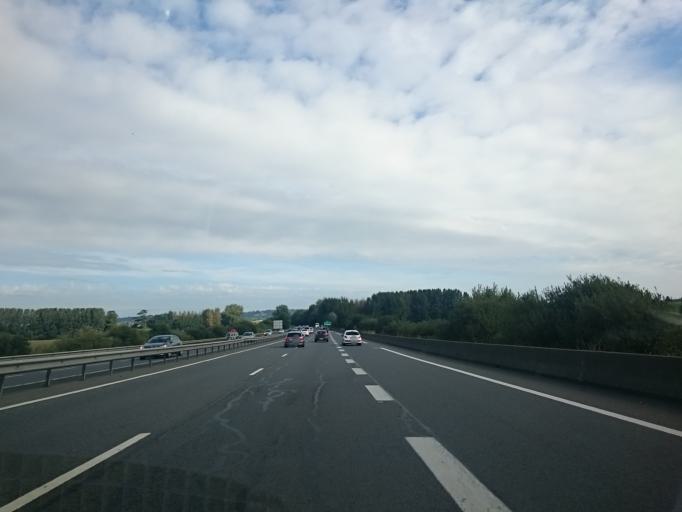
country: FR
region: Lower Normandy
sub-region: Departement de la Manche
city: Saint-Quentin-sur-le-Homme
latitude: 48.6351
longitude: -1.3411
